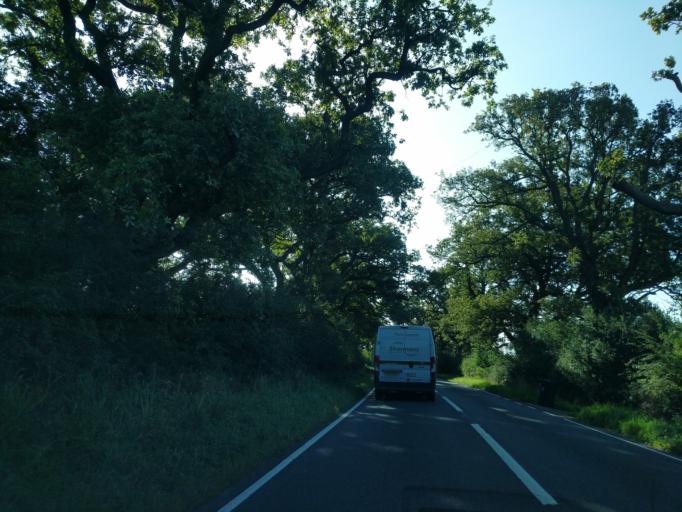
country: GB
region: England
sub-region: Lincolnshire
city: Bourne
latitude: 52.7996
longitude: -0.4703
